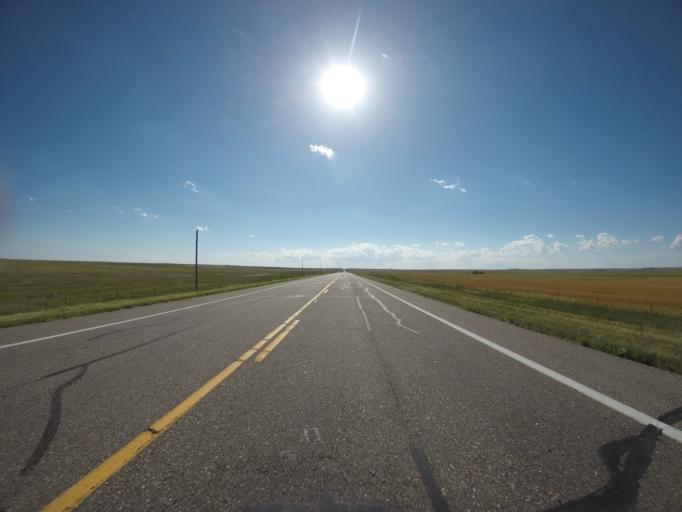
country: US
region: Colorado
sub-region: Logan County
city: Sterling
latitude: 40.6108
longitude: -103.5349
